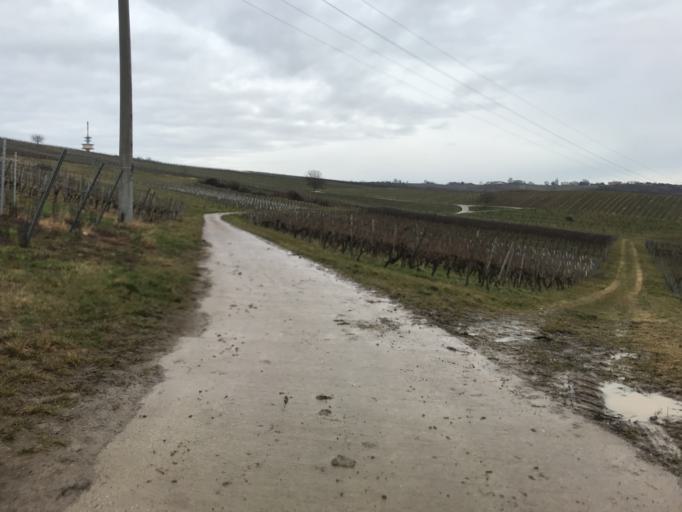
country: DE
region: Rheinland-Pfalz
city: Essenheim
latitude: 49.9311
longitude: 8.1667
